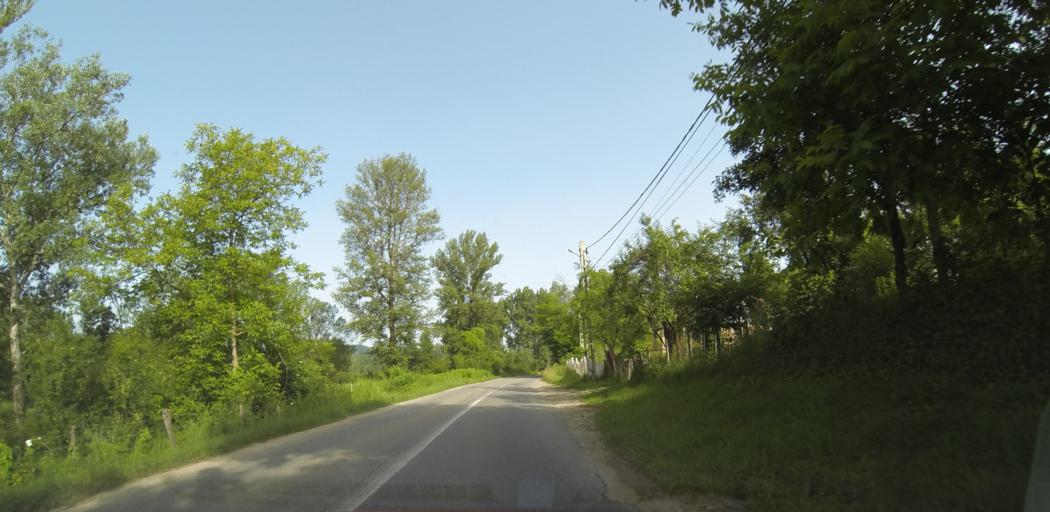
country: RO
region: Valcea
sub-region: Comuna Pausesti-Maglasi
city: Pausesti-Maglasi
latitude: 45.1306
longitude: 24.2616
